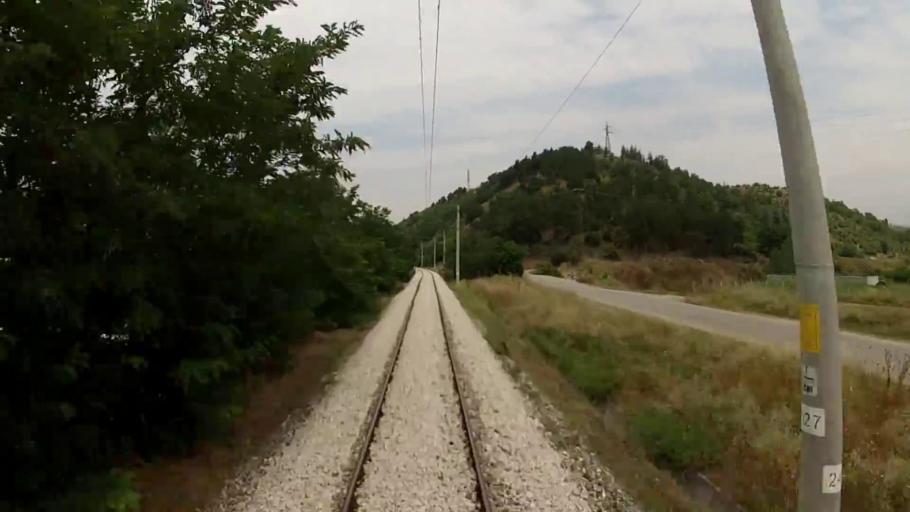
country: BG
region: Blagoevgrad
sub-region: Obshtina Blagoevgrad
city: Blagoevgrad
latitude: 41.9663
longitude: 23.0990
